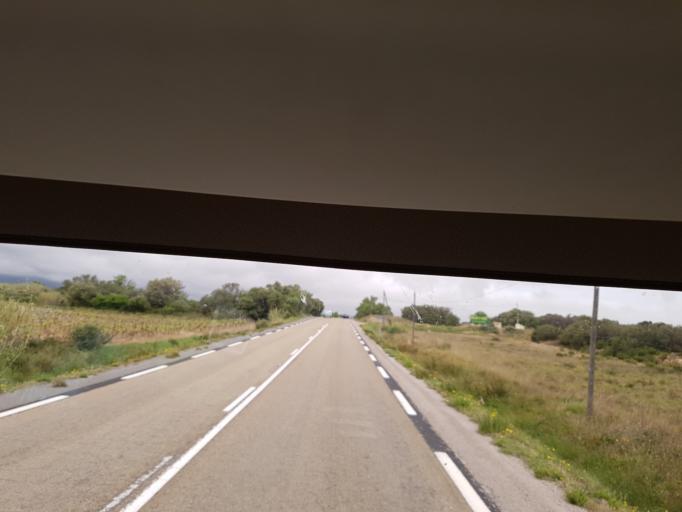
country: FR
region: Languedoc-Roussillon
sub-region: Departement de l'Aude
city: Leucate
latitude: 42.9172
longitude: 2.9970
